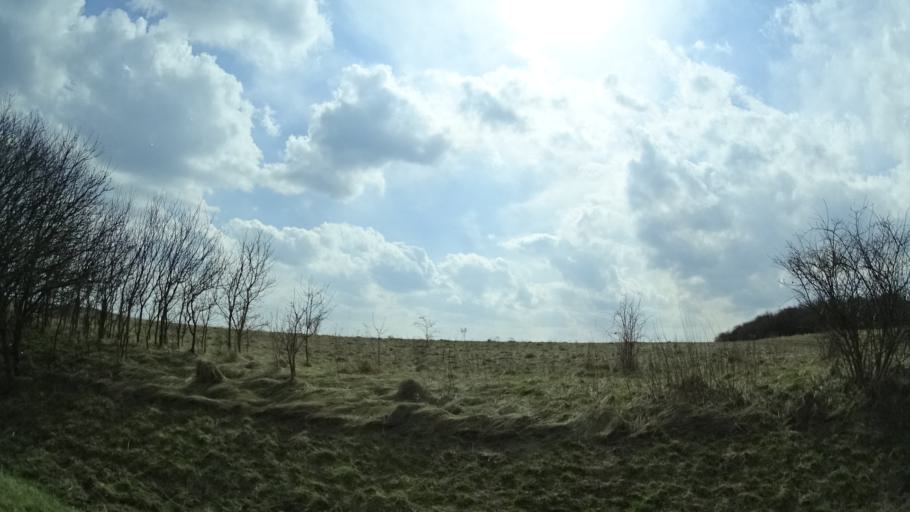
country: DE
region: Saxony-Anhalt
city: Eckartsberga
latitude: 51.1174
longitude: 11.5878
